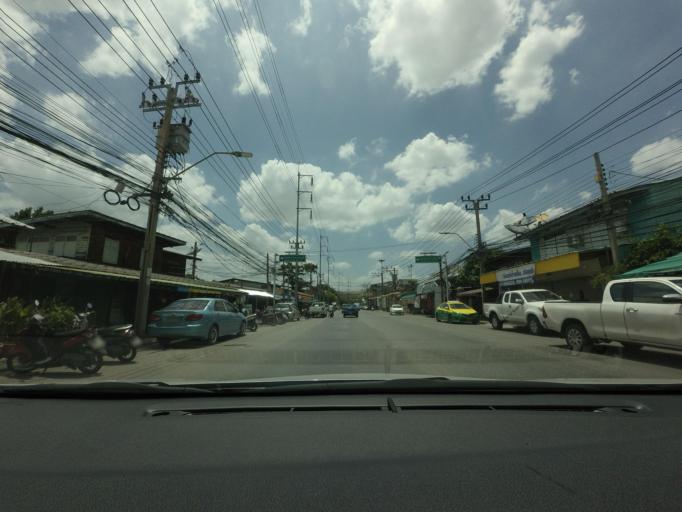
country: TH
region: Samut Prakan
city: Samut Prakan
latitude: 13.5795
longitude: 100.5925
